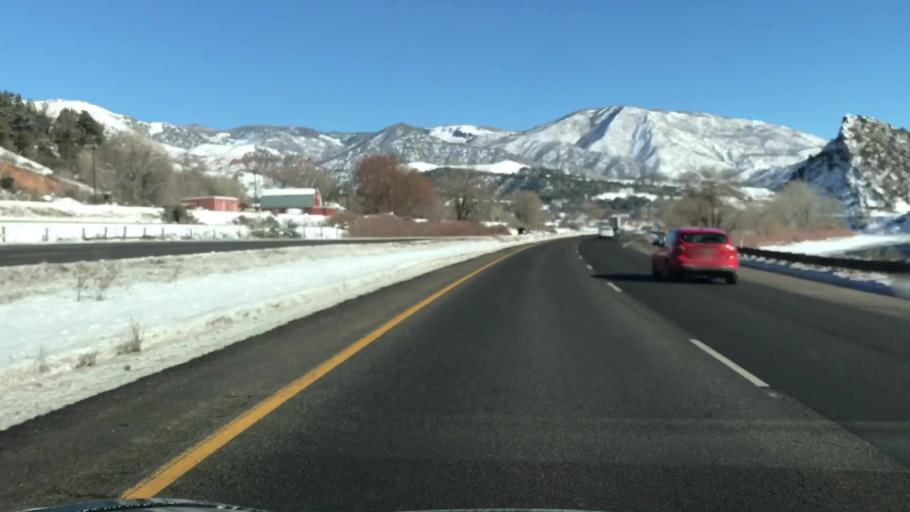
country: US
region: Colorado
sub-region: Garfield County
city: New Castle
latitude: 39.5718
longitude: -107.4804
